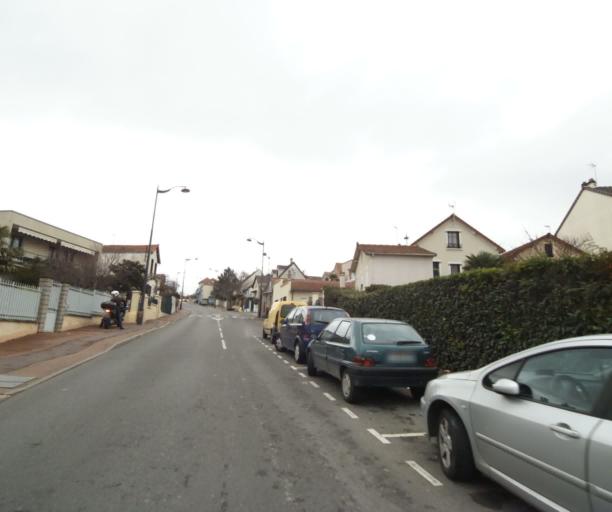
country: FR
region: Ile-de-France
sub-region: Departement des Hauts-de-Seine
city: Rueil-Malmaison
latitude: 48.8781
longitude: 2.1947
